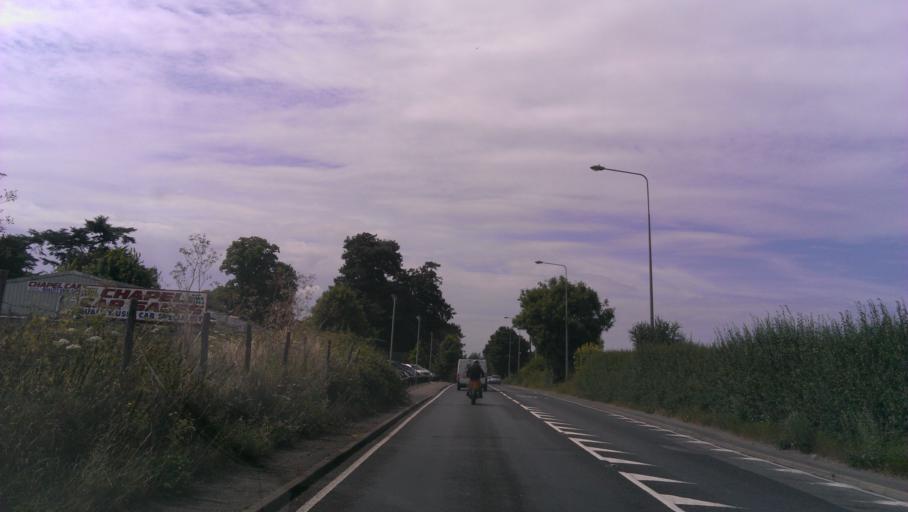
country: GB
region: England
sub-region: Kent
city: Faversham
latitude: 51.3124
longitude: 0.8697
